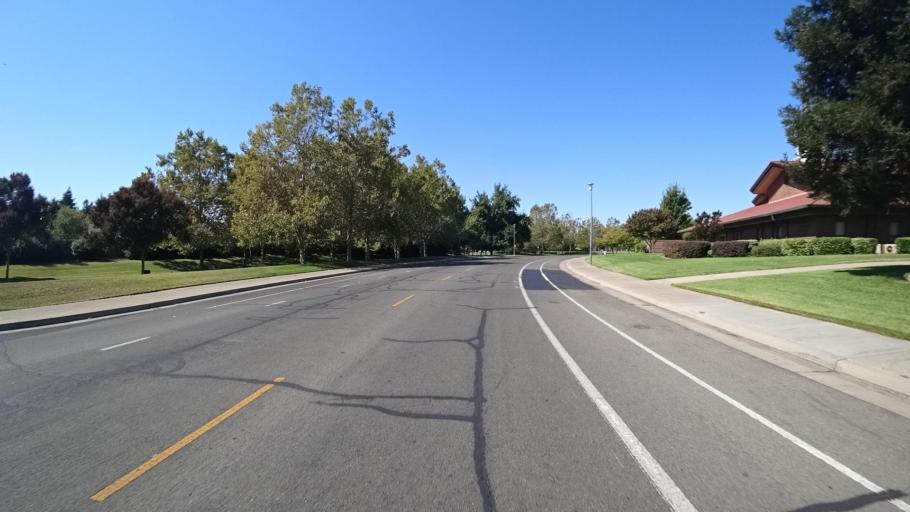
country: US
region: California
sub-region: Sacramento County
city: Laguna
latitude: 38.4194
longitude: -121.4248
